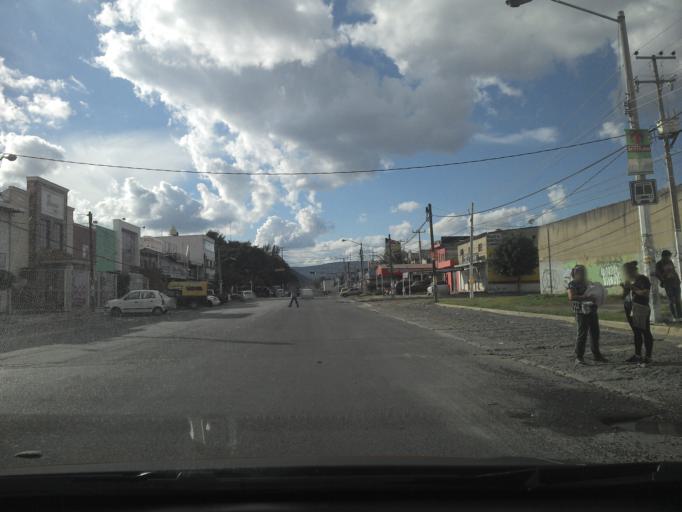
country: MX
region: Jalisco
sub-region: Tlajomulco de Zuniga
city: La Tijera
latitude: 20.6127
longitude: -103.4299
